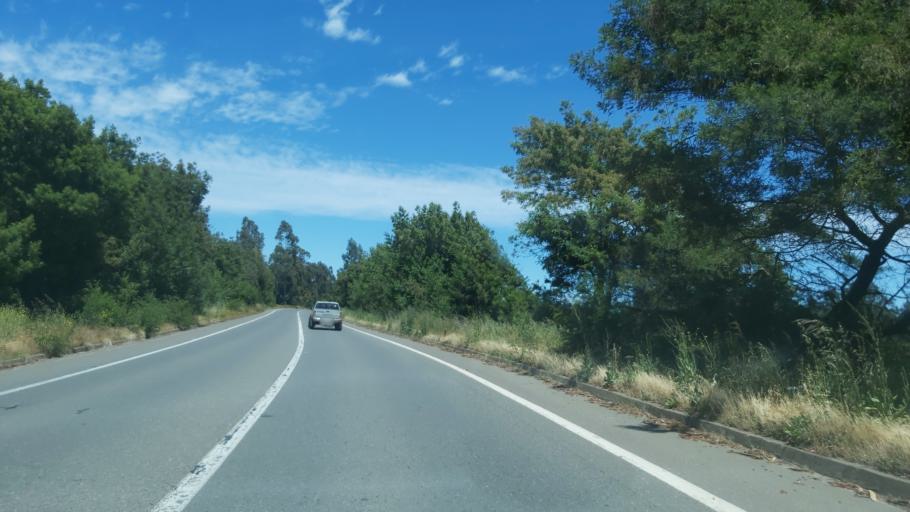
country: CL
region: Maule
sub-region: Provincia de Talca
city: Constitucion
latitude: -35.3011
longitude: -72.3746
